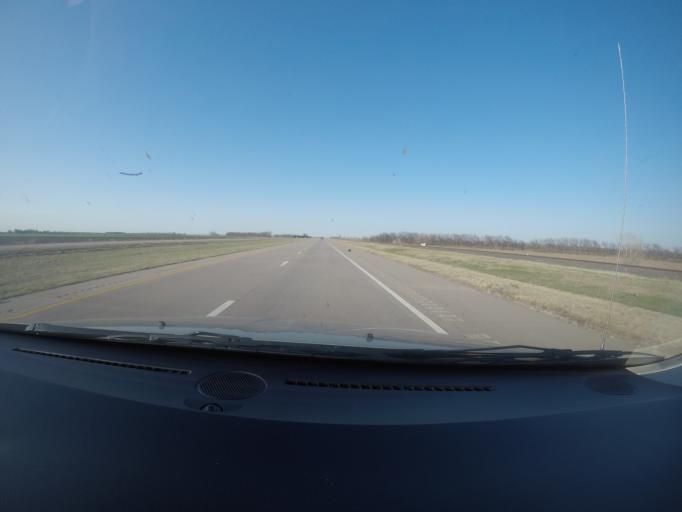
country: US
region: Kansas
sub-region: McPherson County
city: Inman
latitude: 38.2650
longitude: -97.7529
